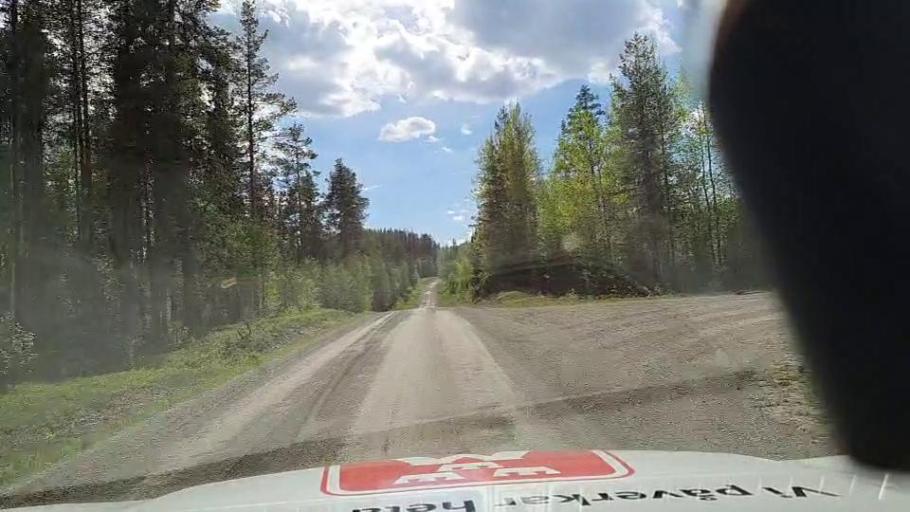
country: SE
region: Vaesterbotten
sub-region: Vilhelmina Kommun
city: Sjoberg
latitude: 64.5668
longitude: 15.8528
